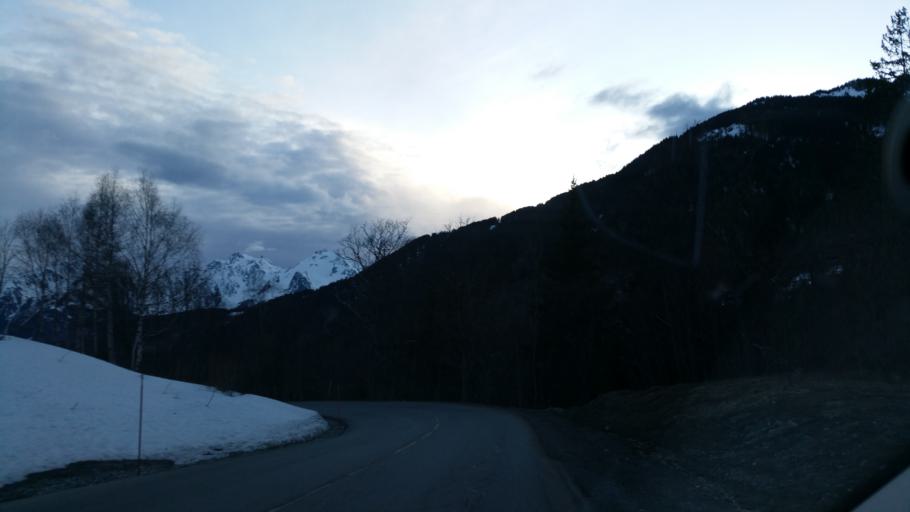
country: FR
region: Rhone-Alpes
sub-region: Departement de la Savoie
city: La Chambre
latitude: 45.4108
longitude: 6.3477
